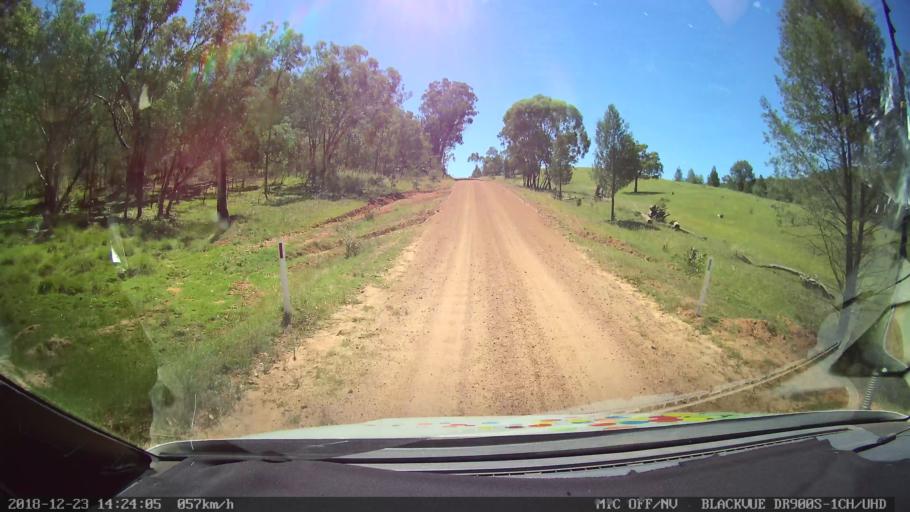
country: AU
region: New South Wales
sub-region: Tamworth Municipality
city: Manilla
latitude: -30.6328
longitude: 150.9633
